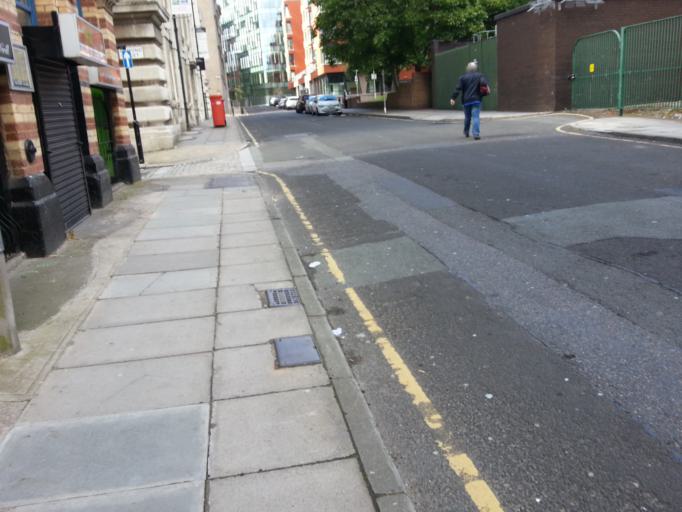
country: GB
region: England
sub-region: Liverpool
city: Liverpool
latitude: 53.4094
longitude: -2.9919
